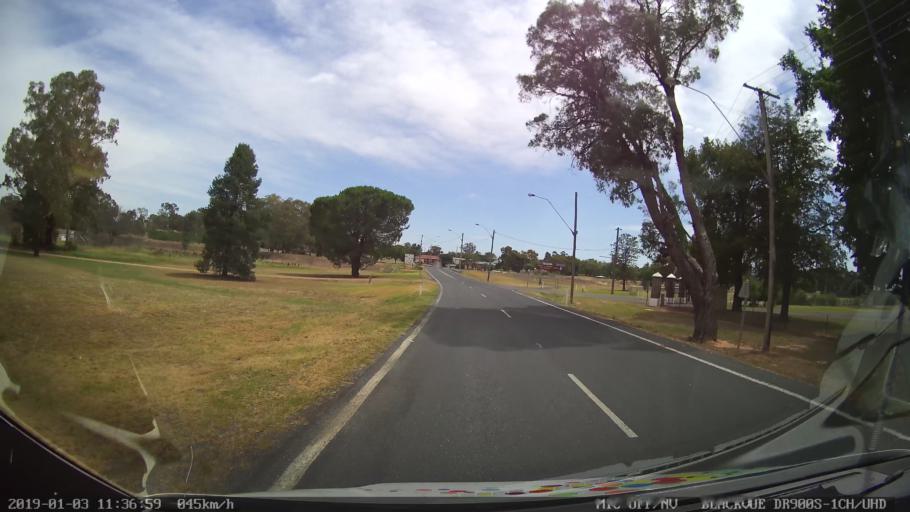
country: AU
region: New South Wales
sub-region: Weddin
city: Grenfell
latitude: -33.9059
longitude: 148.1603
